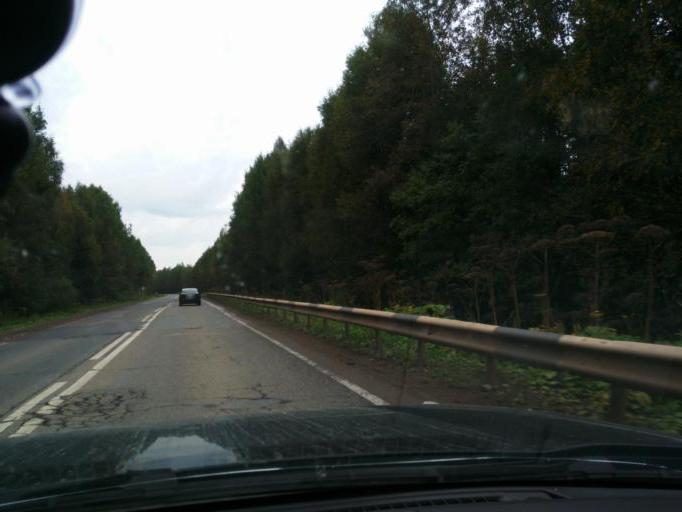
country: RU
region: Perm
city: Chernushka
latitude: 56.6994
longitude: 56.1828
